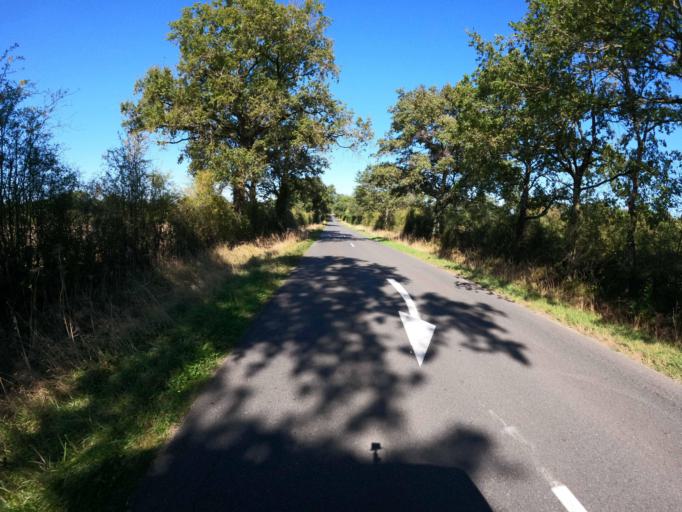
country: FR
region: Poitou-Charentes
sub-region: Departement de la Vienne
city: Lathus-Saint-Remy
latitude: 46.3257
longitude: 0.9677
